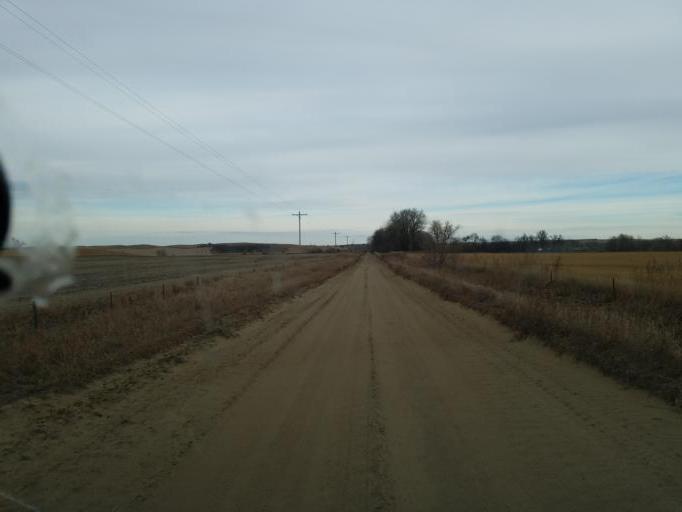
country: US
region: Nebraska
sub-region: Knox County
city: Bloomfield
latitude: 42.5424
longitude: -97.7204
